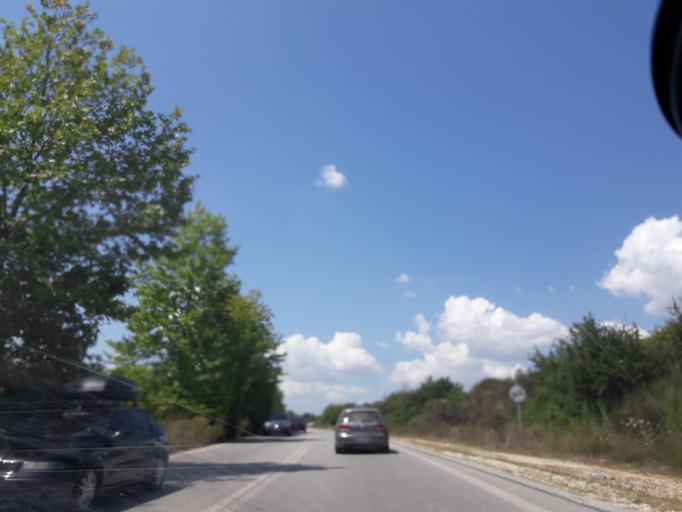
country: GR
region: Central Macedonia
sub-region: Nomos Chalkidikis
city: Galatista
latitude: 40.4653
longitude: 23.3651
